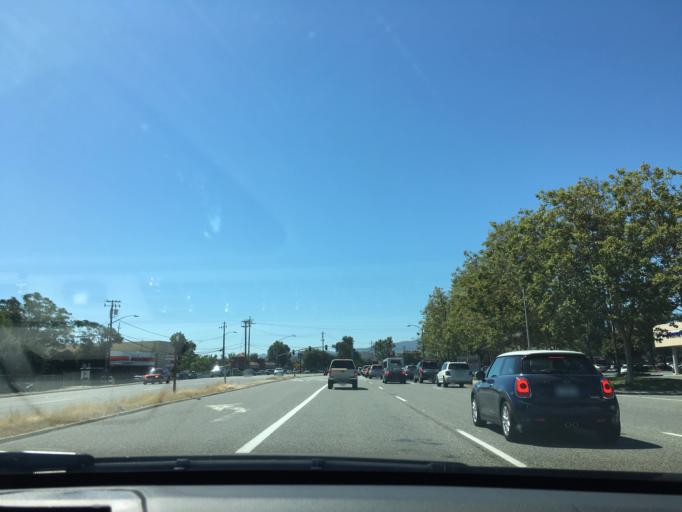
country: US
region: California
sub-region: Santa Clara County
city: Seven Trees
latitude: 37.2646
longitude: -121.8775
